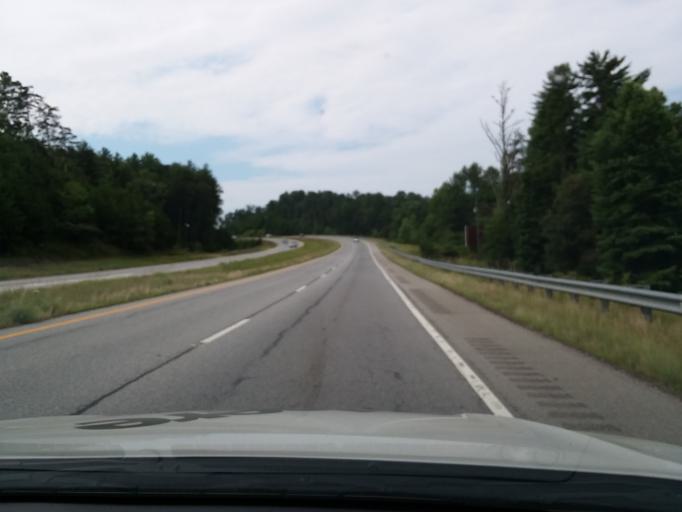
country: US
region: Georgia
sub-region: Rabun County
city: Clayton
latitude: 34.8065
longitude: -83.4261
